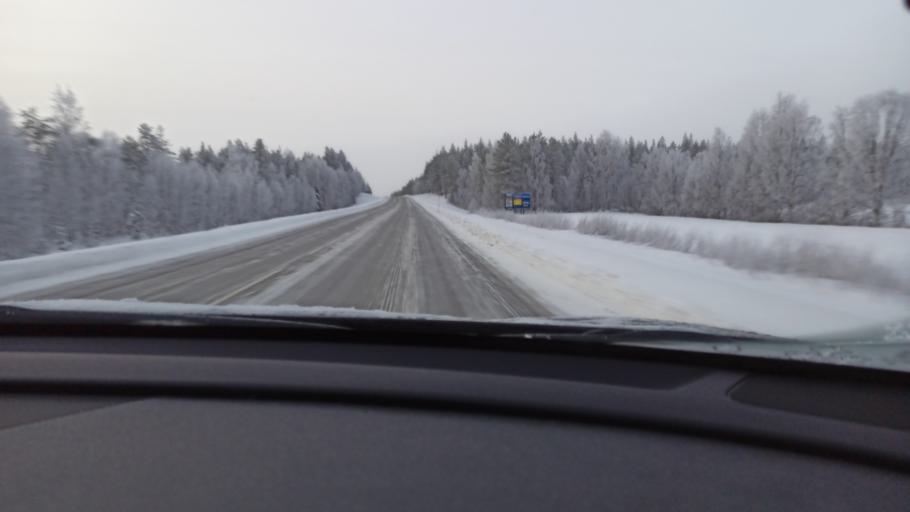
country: FI
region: Lapland
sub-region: Pohjois-Lappi
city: Sodankylae
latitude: 66.9825
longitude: 26.3305
